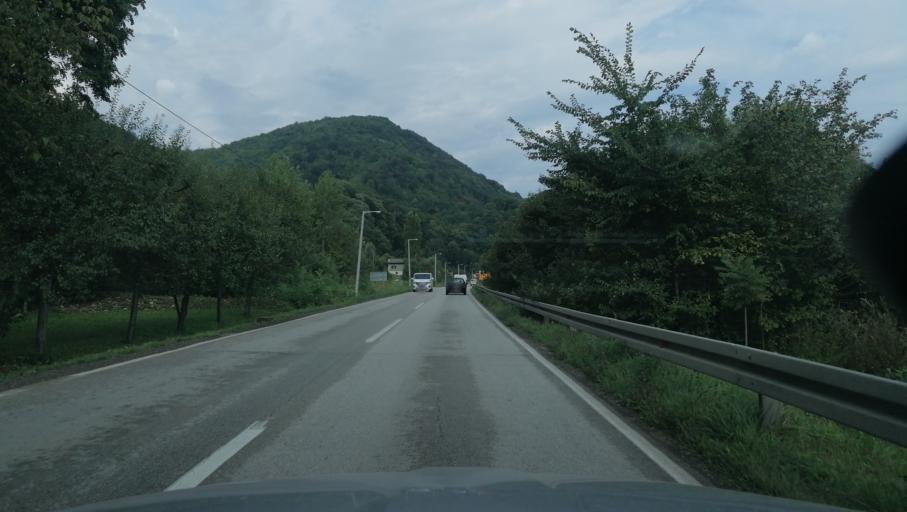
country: BA
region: Republika Srpska
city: Hiseti
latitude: 44.7073
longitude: 17.1728
